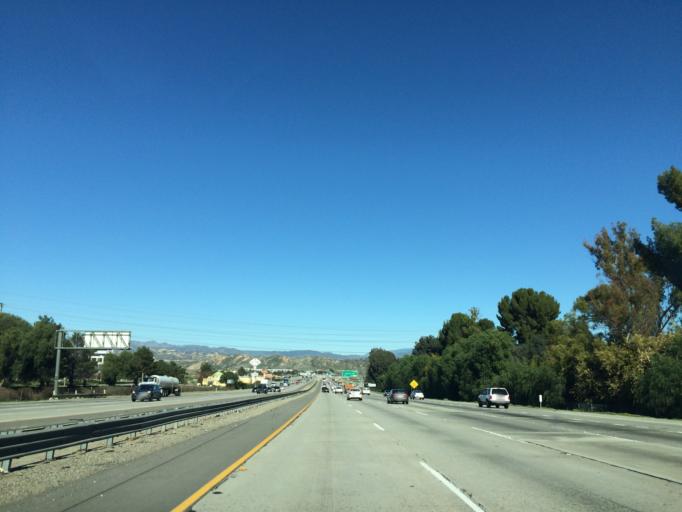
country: US
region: California
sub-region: Los Angeles County
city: Valencia
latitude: 34.4162
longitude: -118.5793
